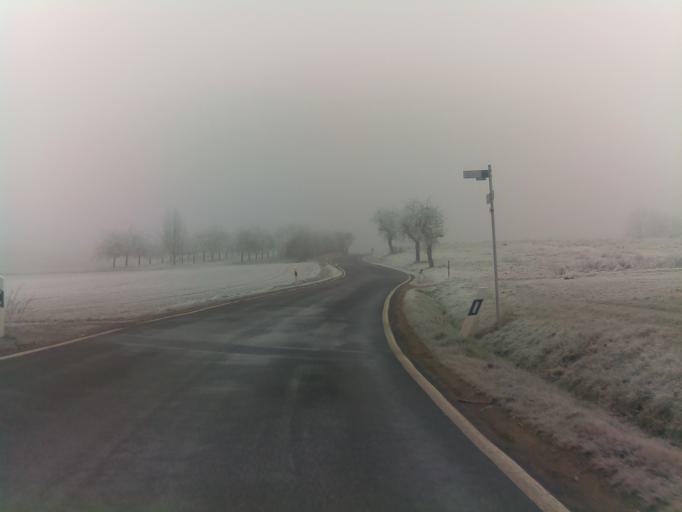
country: DE
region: Bavaria
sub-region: Regierungsbezirk Unterfranken
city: Donnersdorf
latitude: 49.9657
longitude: 10.4213
